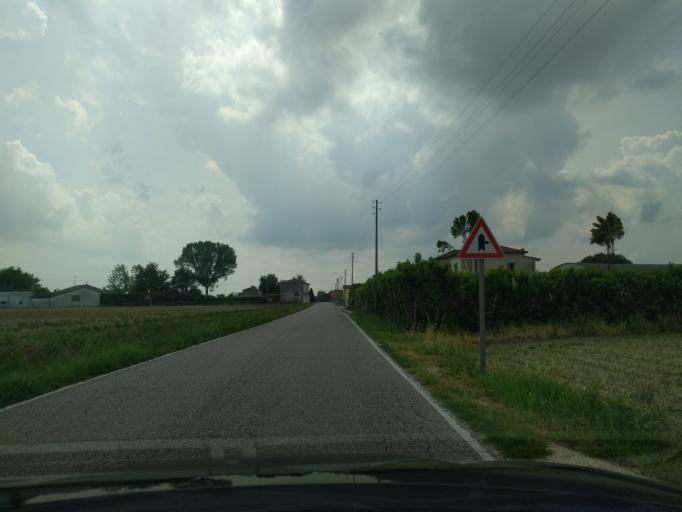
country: IT
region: Veneto
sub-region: Provincia di Rovigo
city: Lendinara
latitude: 45.0884
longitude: 11.5616
